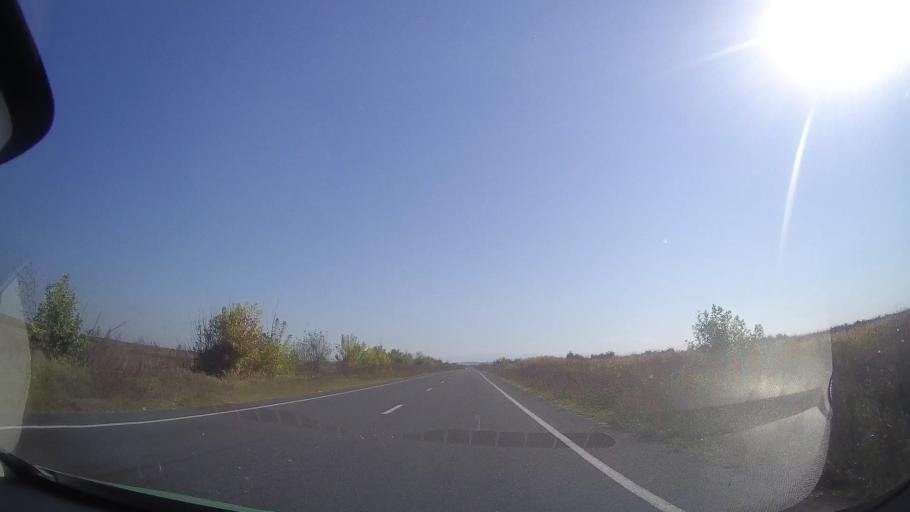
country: RO
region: Timis
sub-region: Comuna Costeiu
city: Costeiu
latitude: 45.7444
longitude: 21.8092
